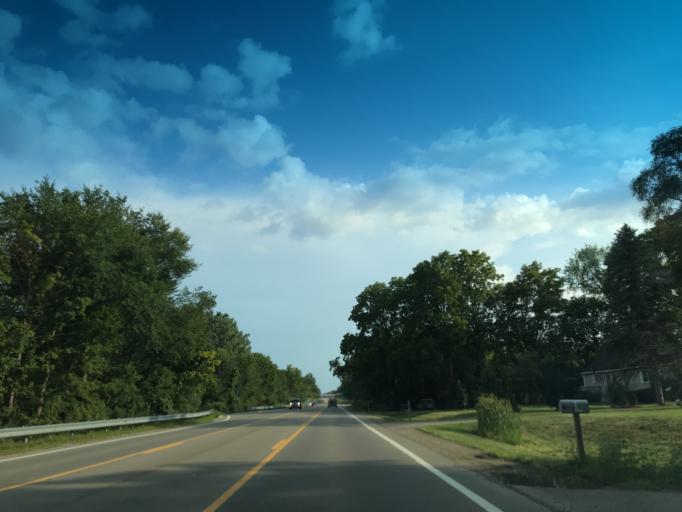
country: US
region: Michigan
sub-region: Oakland County
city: Milford
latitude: 42.5416
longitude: -83.6173
